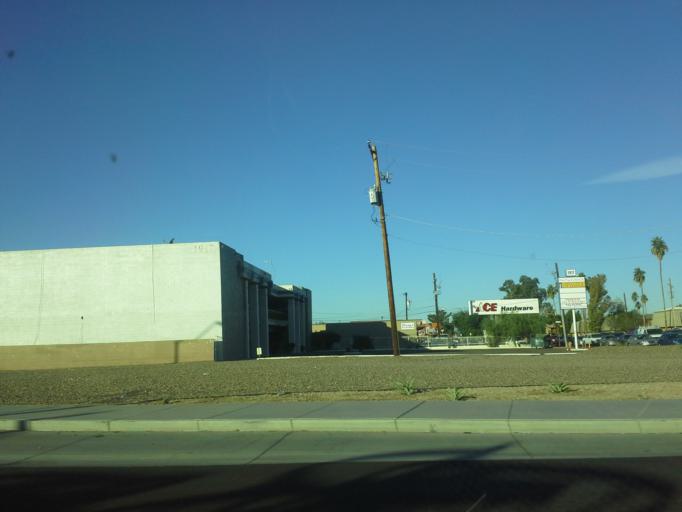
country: US
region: Arizona
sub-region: Maricopa County
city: Glendale
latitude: 33.5394
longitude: -112.1012
